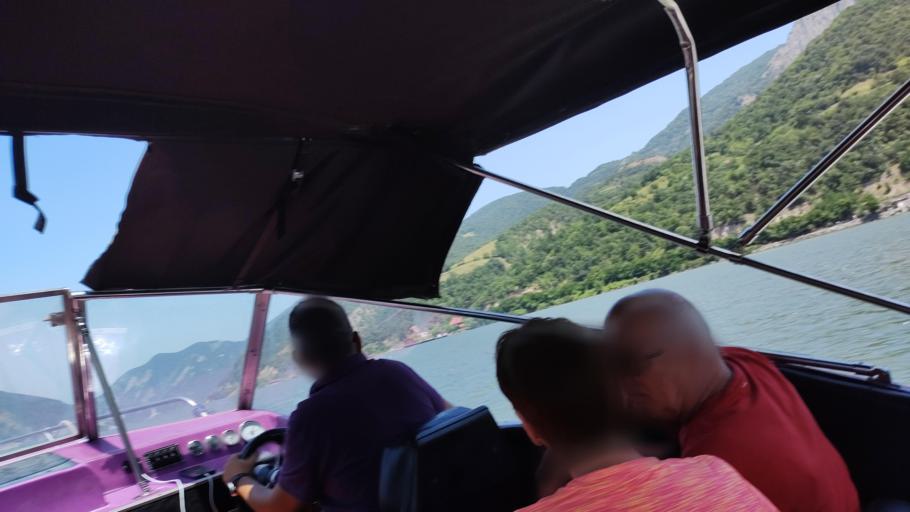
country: RO
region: Mehedinti
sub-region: Comuna Svinita
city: Svinita
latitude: 44.5525
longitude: 22.0333
